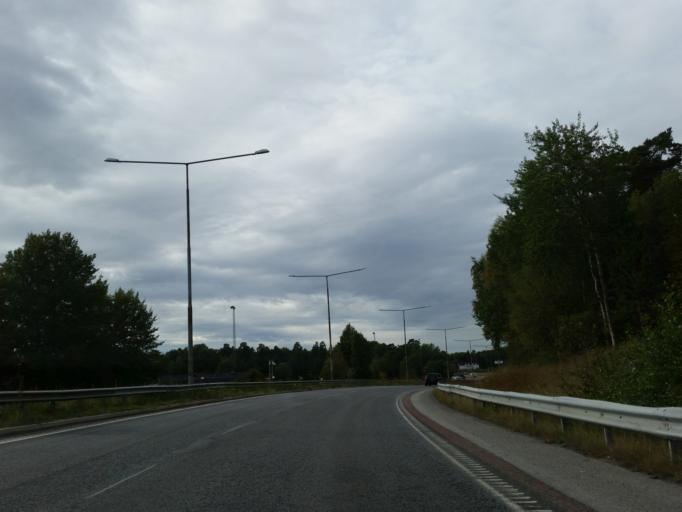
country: SE
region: Stockholm
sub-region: Solna Kommun
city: Rasunda
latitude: 59.3792
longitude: 17.9826
